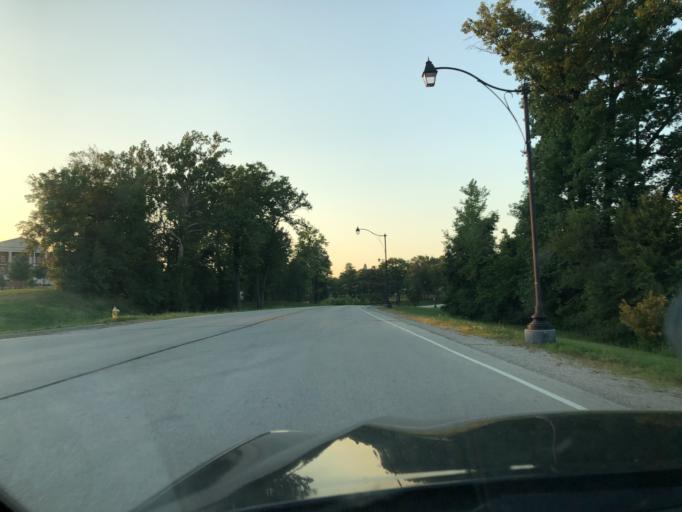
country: US
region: Kansas
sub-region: Leavenworth County
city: Leavenworth
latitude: 39.3421
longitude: -94.9135
